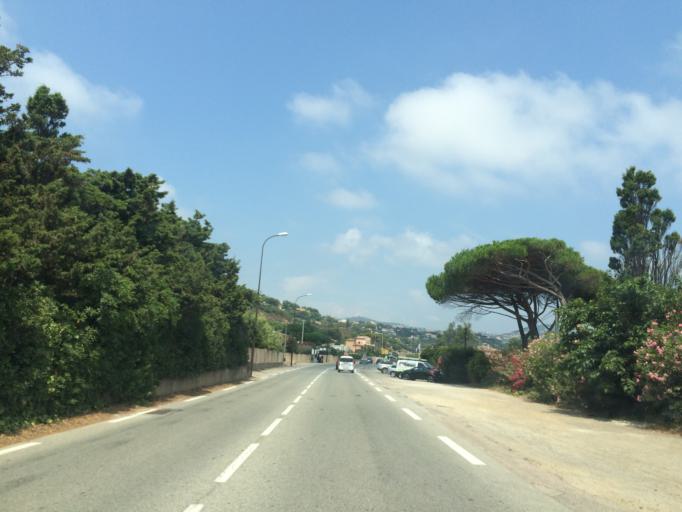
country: FR
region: Provence-Alpes-Cote d'Azur
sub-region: Departement du Var
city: Sainte-Maxime
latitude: 43.3278
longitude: 6.6670
